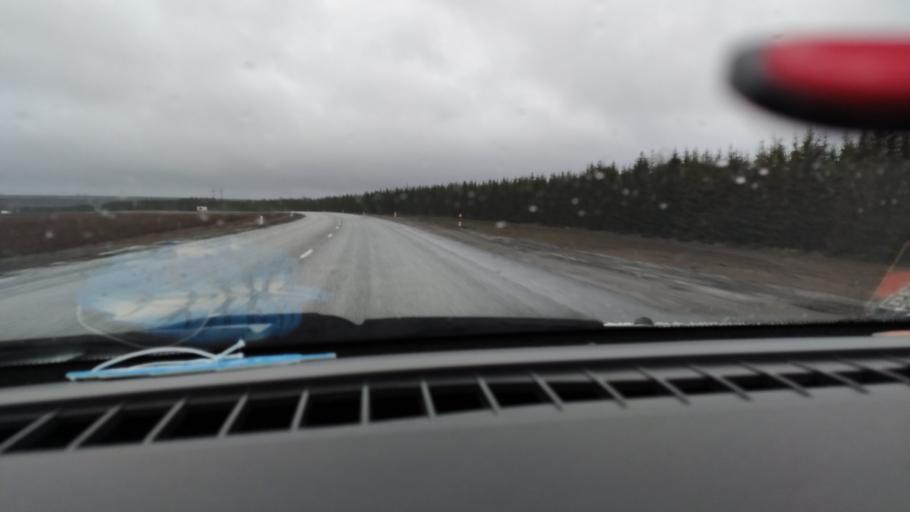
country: RU
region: Udmurtiya
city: Alnashi
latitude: 56.0812
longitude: 52.4042
